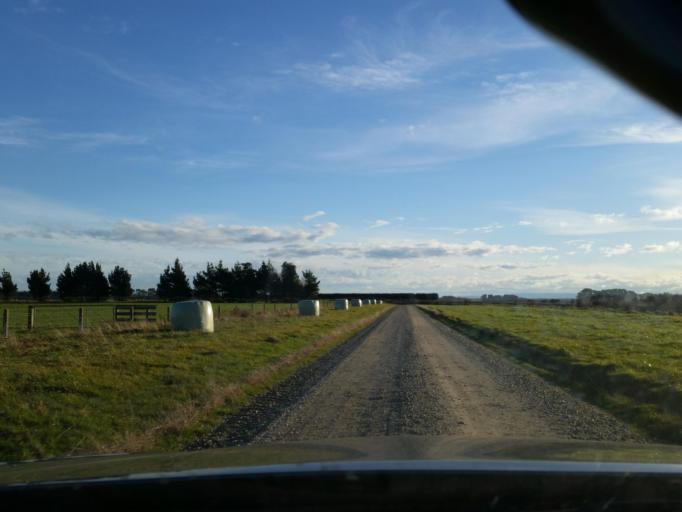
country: NZ
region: Southland
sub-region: Invercargill City
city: Invercargill
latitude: -46.3428
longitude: 168.6125
